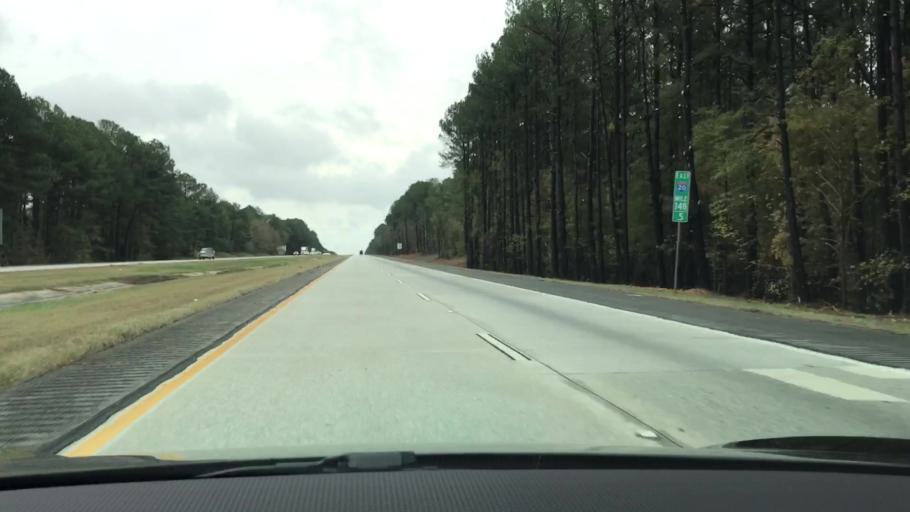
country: US
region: Georgia
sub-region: Taliaferro County
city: Crawfordville
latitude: 33.5285
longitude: -82.8982
